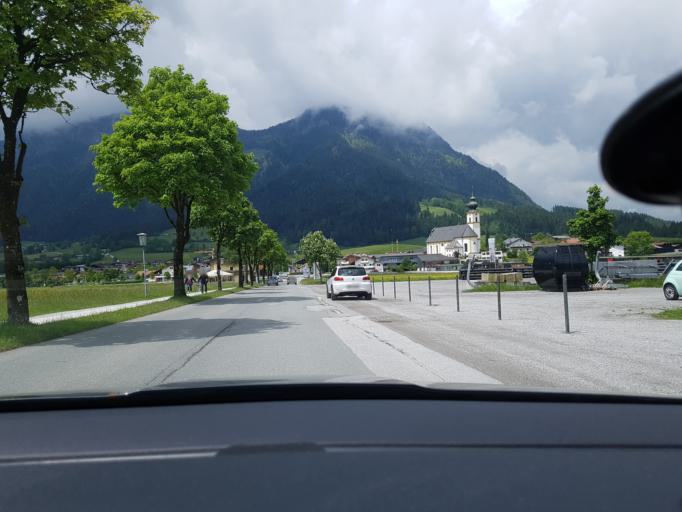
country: AT
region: Tyrol
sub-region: Politischer Bezirk Kufstein
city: Soll
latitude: 47.5006
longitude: 12.1960
